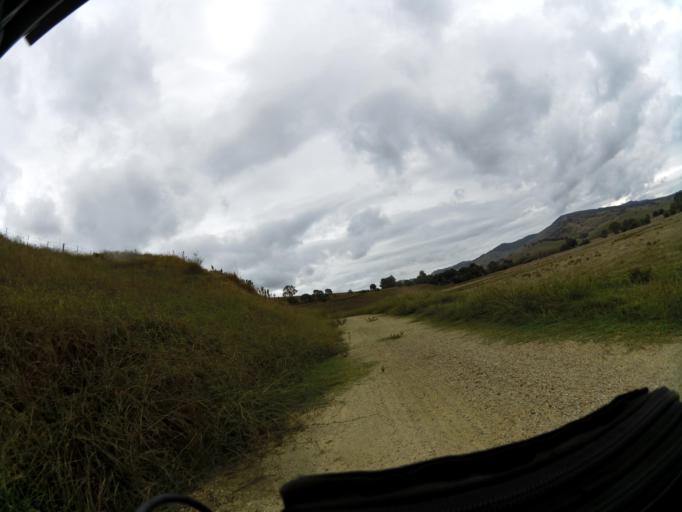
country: AU
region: New South Wales
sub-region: Albury Municipality
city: East Albury
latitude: -36.1925
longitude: 147.2953
